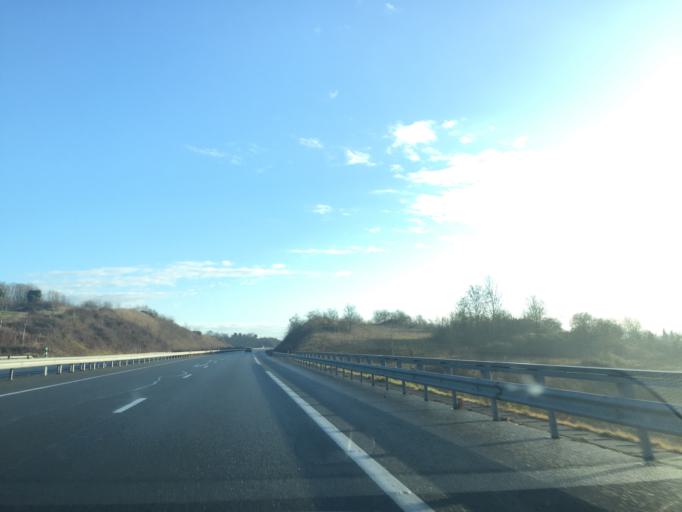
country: FR
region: Aquitaine
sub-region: Departement de la Dordogne
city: Thenon
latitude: 45.1545
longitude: 1.1140
